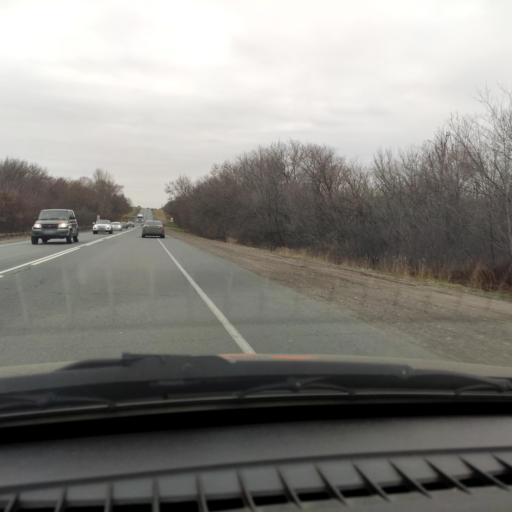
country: RU
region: Samara
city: Zhigulevsk
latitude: 53.3551
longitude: 49.4552
